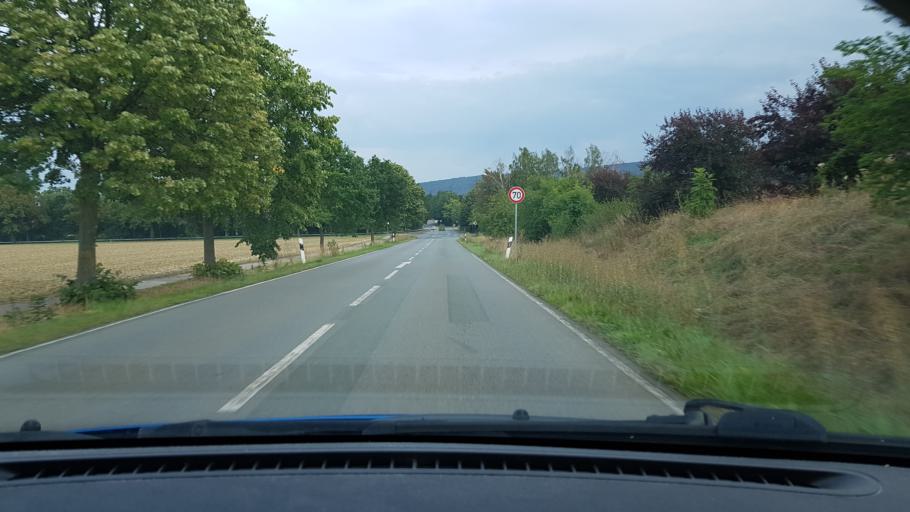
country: DE
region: Lower Saxony
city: Hulsede
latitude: 52.2128
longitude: 9.3911
